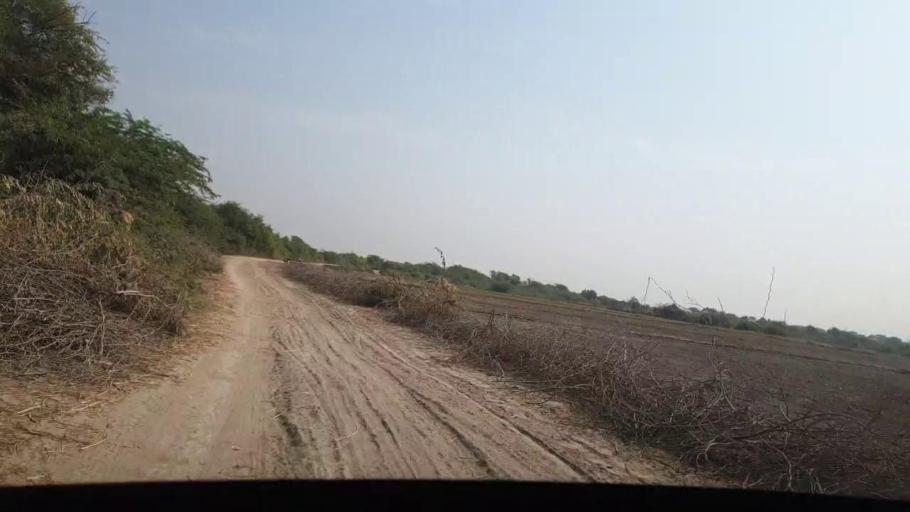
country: PK
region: Sindh
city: Chuhar Jamali
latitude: 24.2694
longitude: 67.9216
